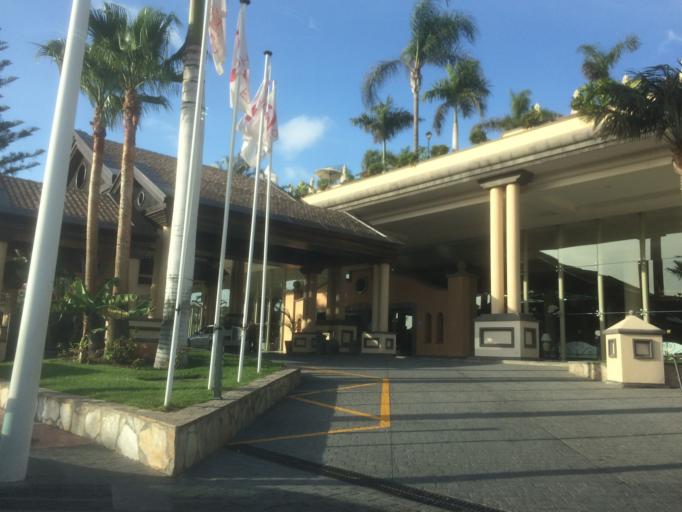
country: ES
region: Canary Islands
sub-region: Provincia de Santa Cruz de Tenerife
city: Playa de las Americas
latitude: 28.0930
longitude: -16.7368
